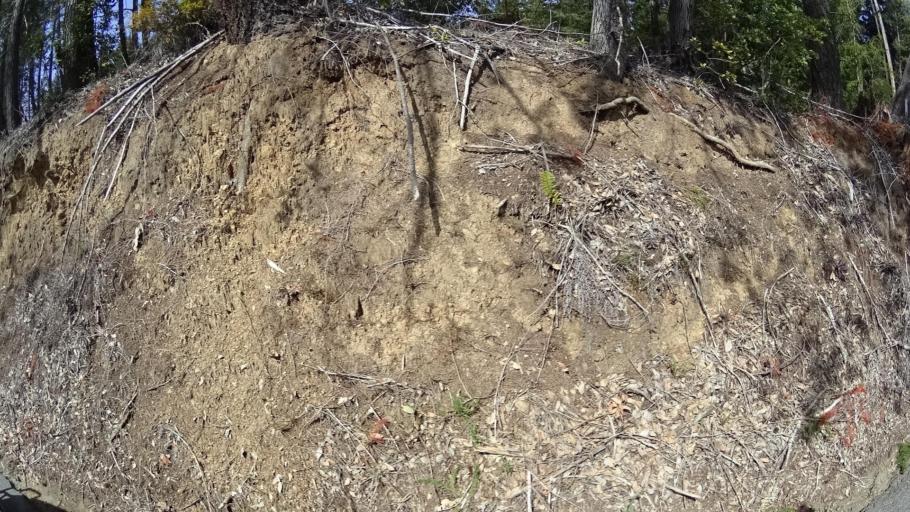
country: US
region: California
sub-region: Humboldt County
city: Redway
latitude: 40.3686
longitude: -123.7338
